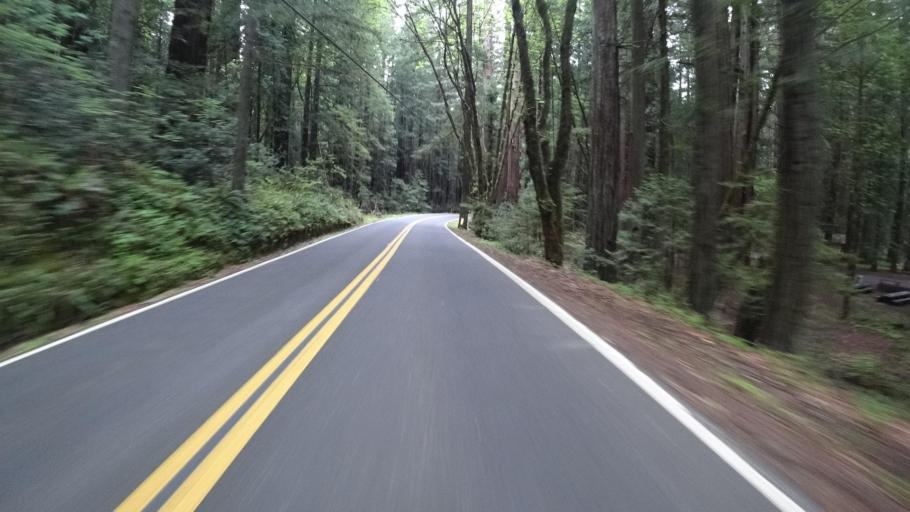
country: US
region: California
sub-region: Humboldt County
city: Redway
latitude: 40.2786
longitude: -123.8884
